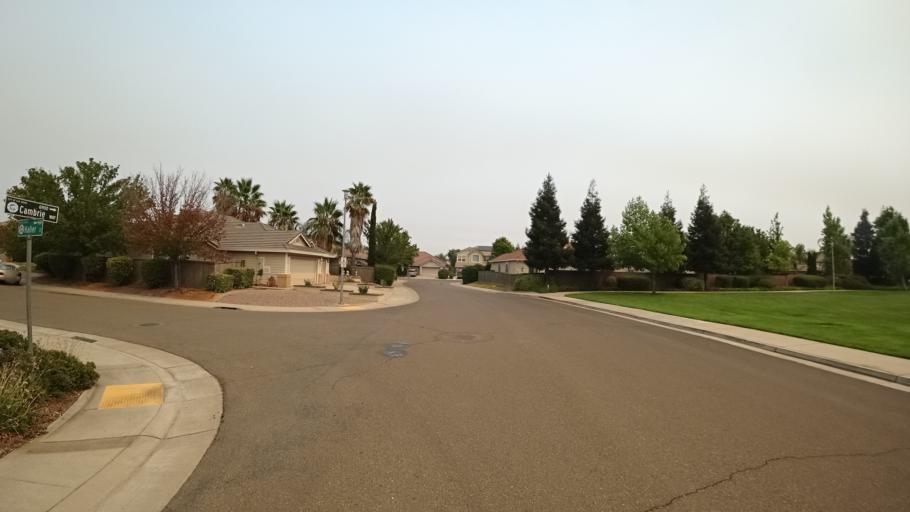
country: US
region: California
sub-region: Sacramento County
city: Laguna
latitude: 38.4064
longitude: -121.4230
